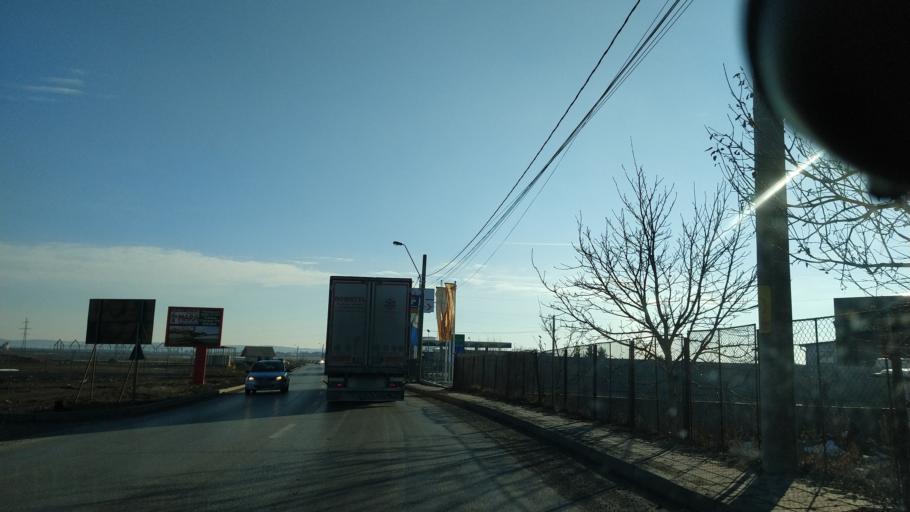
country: RO
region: Neamt
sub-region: Municipiul Roman
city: Roman
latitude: 46.9261
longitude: 26.9089
